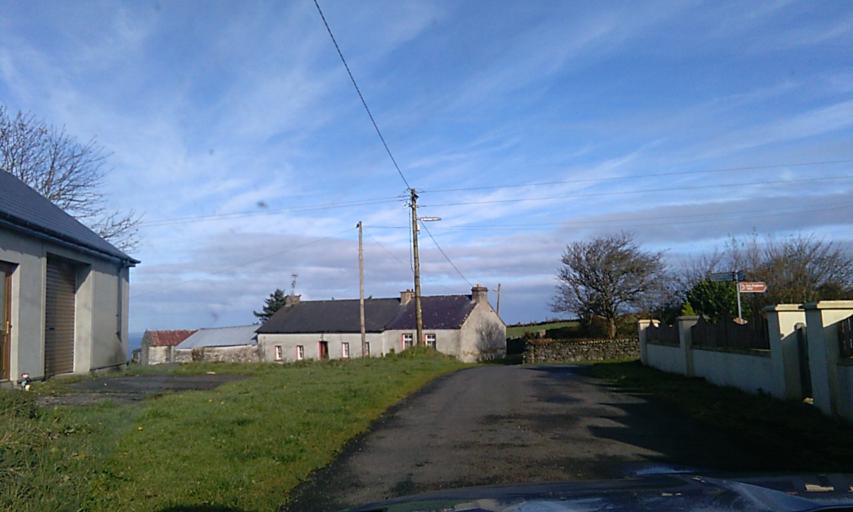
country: IE
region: Ulster
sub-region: County Donegal
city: Moville
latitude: 55.2681
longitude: -7.0550
